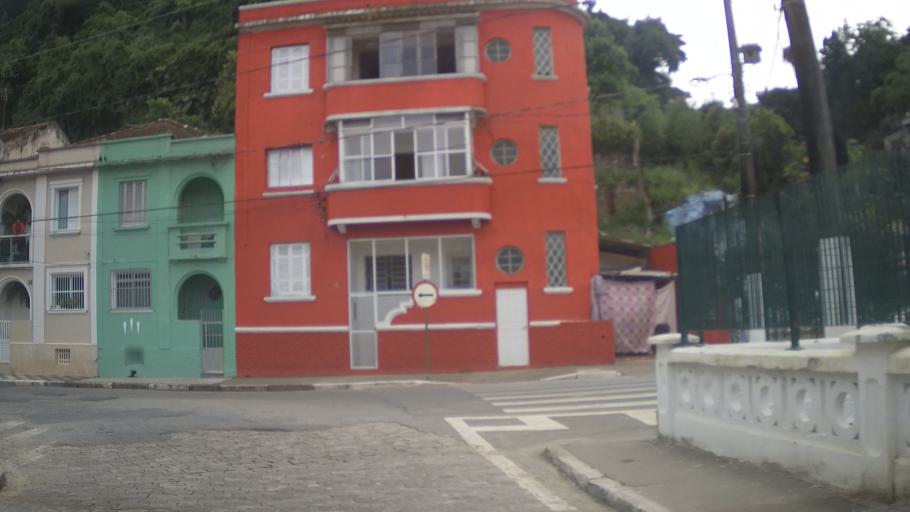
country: BR
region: Sao Paulo
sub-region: Santos
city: Santos
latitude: -23.9660
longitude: -46.3529
